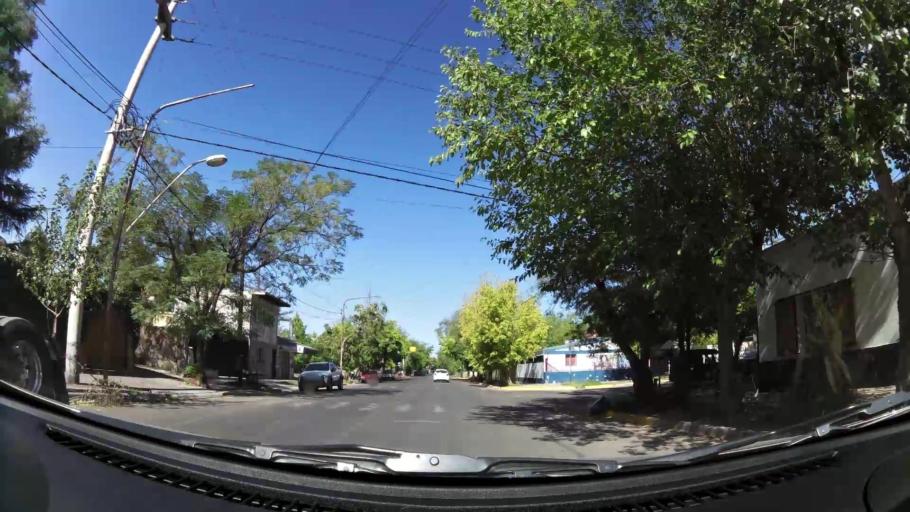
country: AR
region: Mendoza
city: Villa Nueva
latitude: -32.8977
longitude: -68.7903
